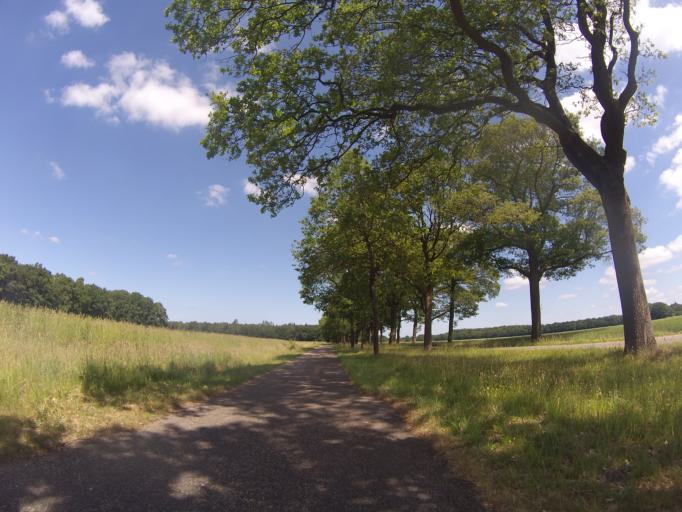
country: NL
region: Drenthe
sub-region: Gemeente Borger-Odoorn
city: Borger
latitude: 52.8647
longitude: 6.8567
